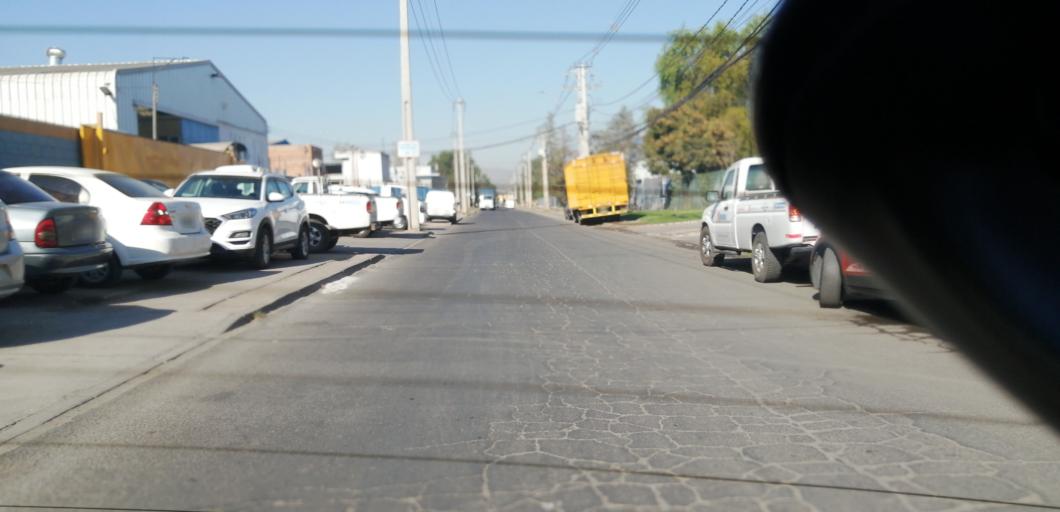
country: CL
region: Santiago Metropolitan
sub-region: Provincia de Santiago
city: Lo Prado
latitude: -33.3781
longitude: -70.7672
